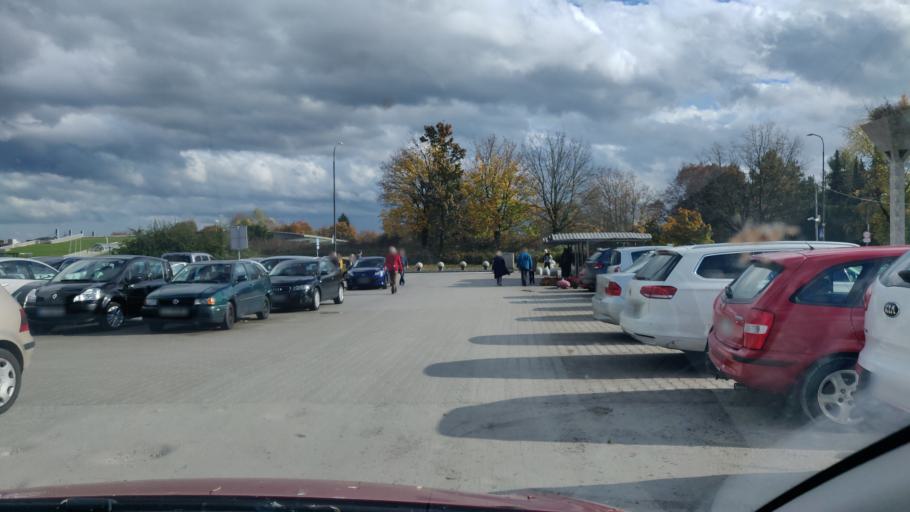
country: SI
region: Ljubljana
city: Ljubljana
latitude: 46.0745
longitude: 14.5309
